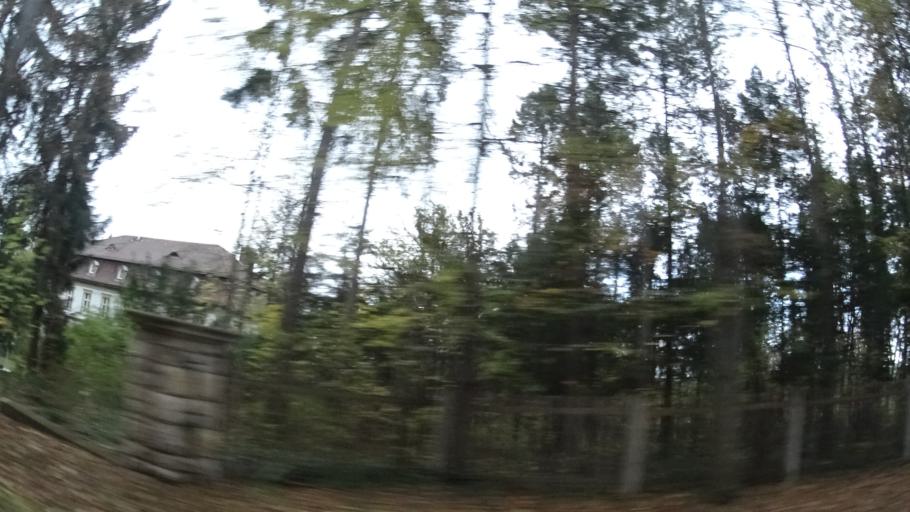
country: DE
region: Thuringia
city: Possneck
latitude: 50.6879
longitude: 11.5993
